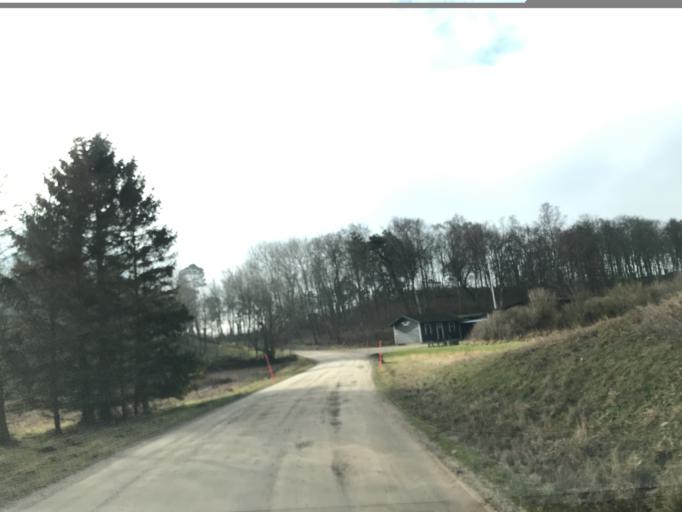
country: SE
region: Skane
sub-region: Svalovs Kommun
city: Teckomatorp
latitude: 55.8325
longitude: 13.0734
